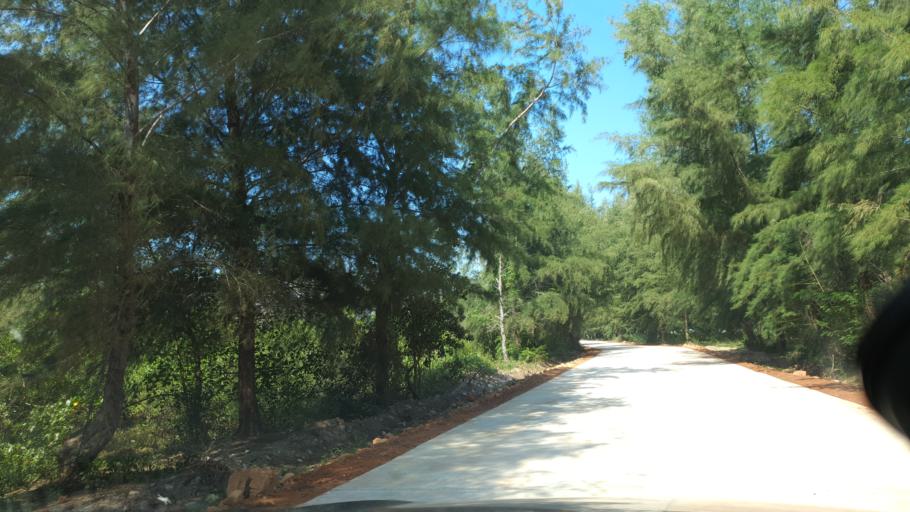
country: TH
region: Surat Thani
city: Tha Chana
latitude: 9.5963
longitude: 99.2091
